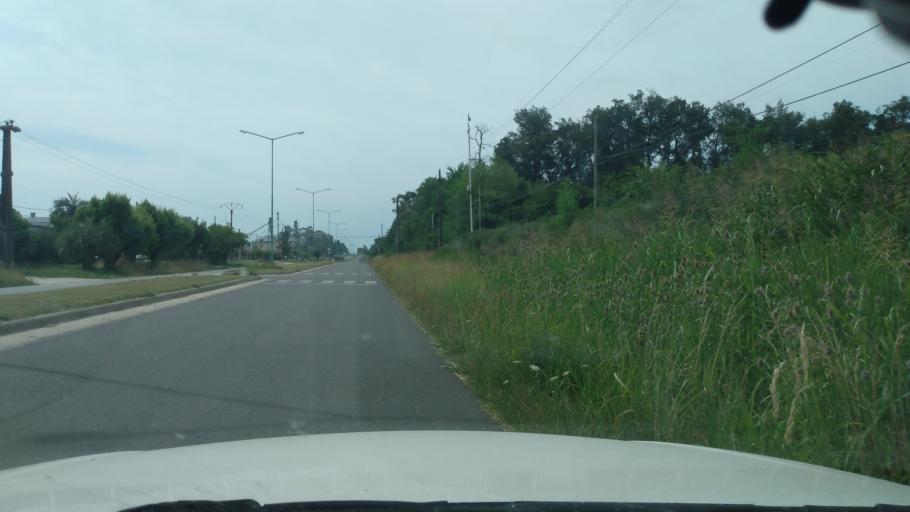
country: AR
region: Buenos Aires
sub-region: Partido de Lujan
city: Lujan
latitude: -34.5549
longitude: -59.1320
